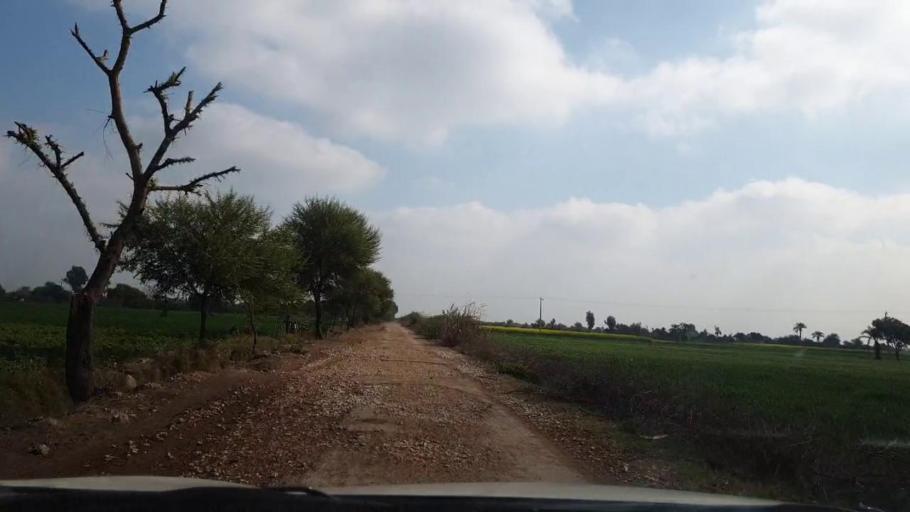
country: PK
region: Sindh
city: Berani
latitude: 25.7774
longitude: 68.9751
